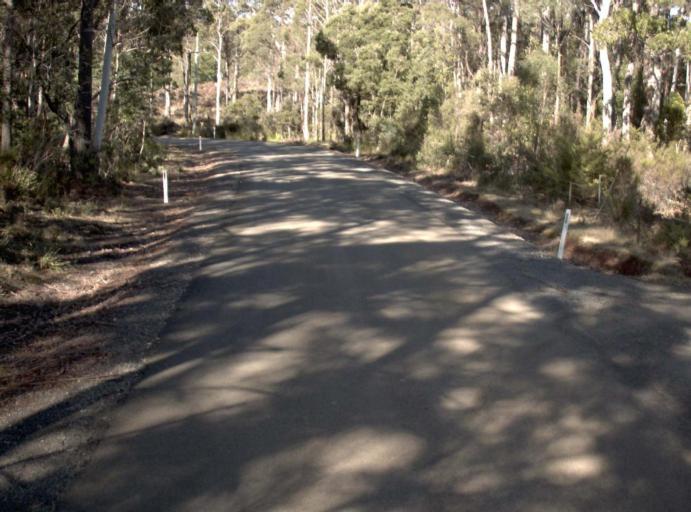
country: AU
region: Tasmania
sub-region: Launceston
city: Mayfield
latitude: -41.3188
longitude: 147.2095
